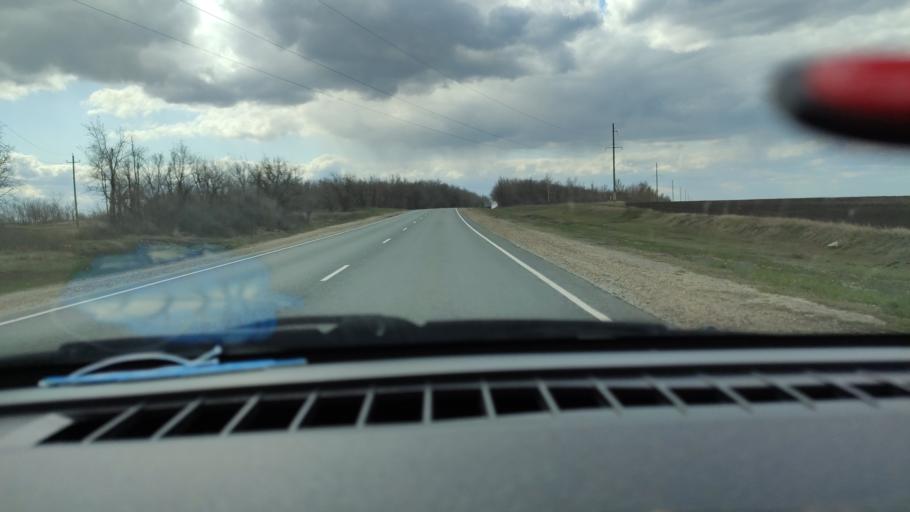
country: RU
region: Saratov
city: Alekseyevka
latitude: 52.2700
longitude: 47.9283
